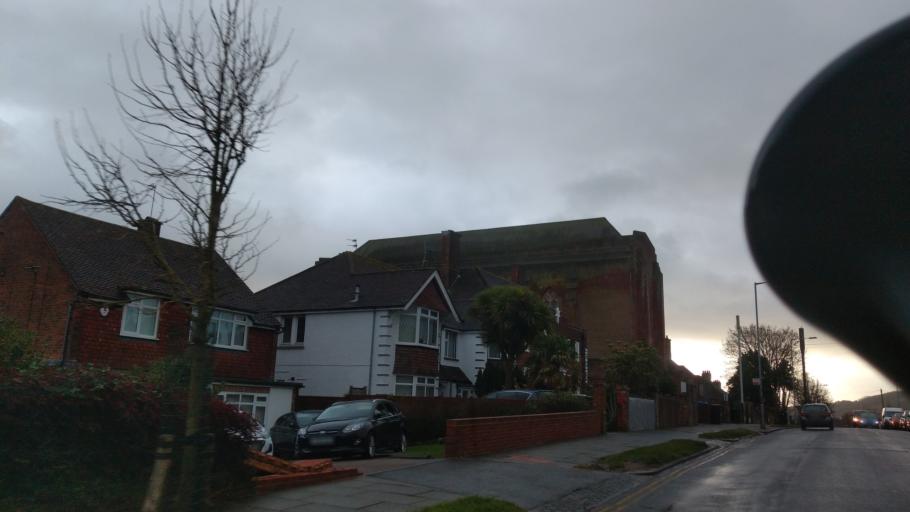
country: GB
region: England
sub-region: East Sussex
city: Eastbourne
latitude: 50.7838
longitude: 0.2542
